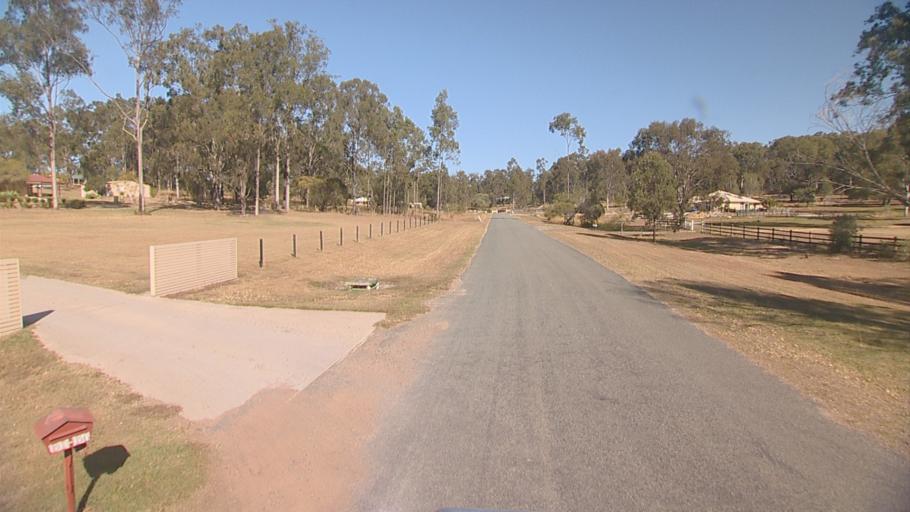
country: AU
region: Queensland
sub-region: Logan
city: Cedar Vale
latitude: -27.8602
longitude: 153.0330
